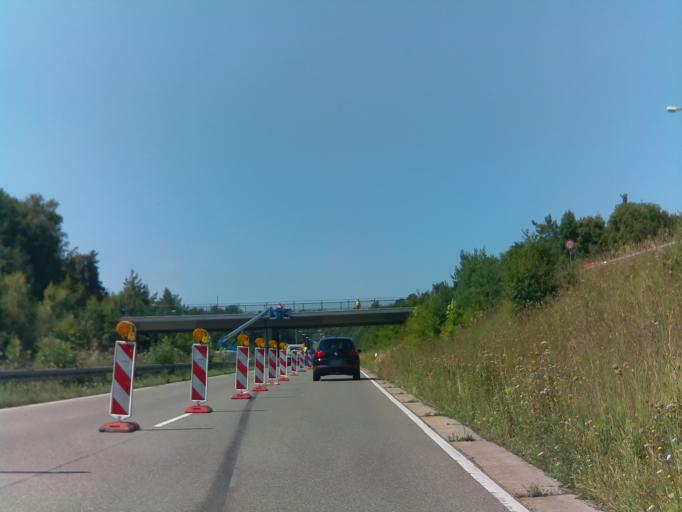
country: DE
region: Baden-Wuerttemberg
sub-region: Regierungsbezirk Stuttgart
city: Gerlingen
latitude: 48.7775
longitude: 9.0918
